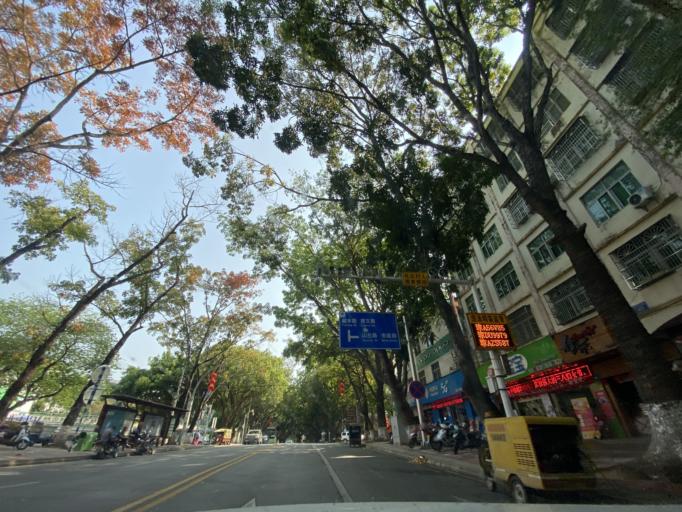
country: CN
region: Hainan
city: Chongshan
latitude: 18.7777
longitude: 109.5145
